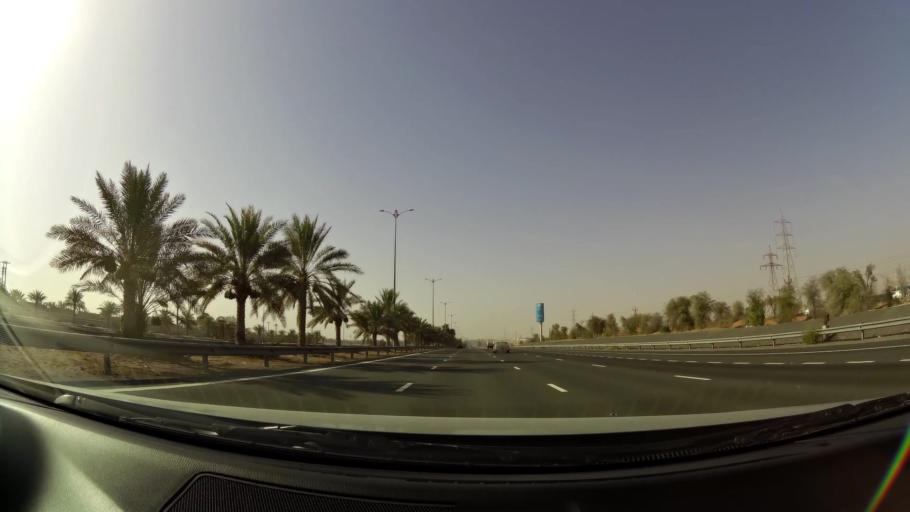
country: OM
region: Al Buraimi
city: Al Buraymi
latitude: 24.4741
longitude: 55.7768
